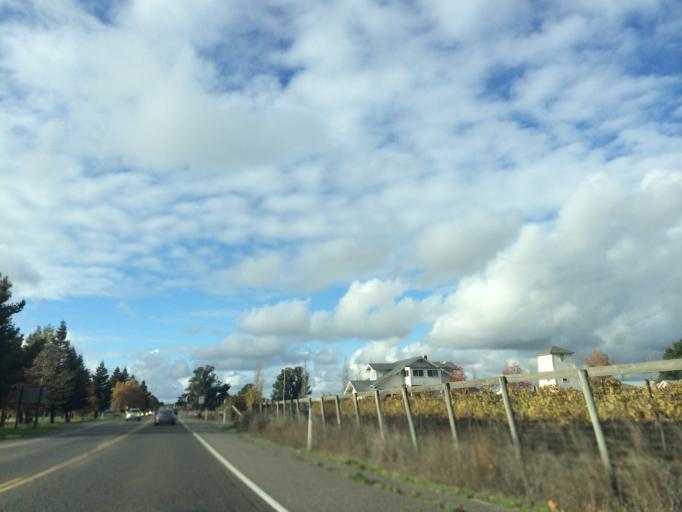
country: US
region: California
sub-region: Sonoma County
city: Petaluma
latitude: 38.2300
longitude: -122.5818
